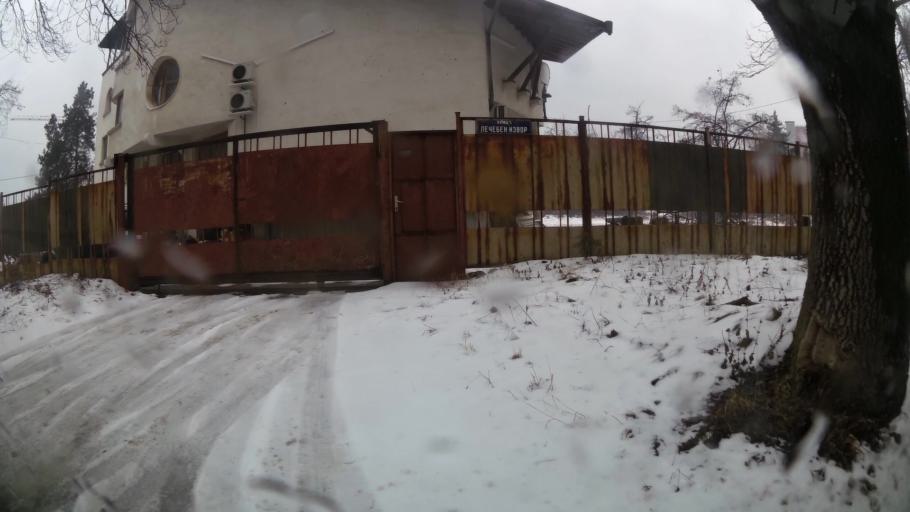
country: BG
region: Sofia-Capital
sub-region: Stolichna Obshtina
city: Sofia
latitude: 42.6779
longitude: 23.2654
